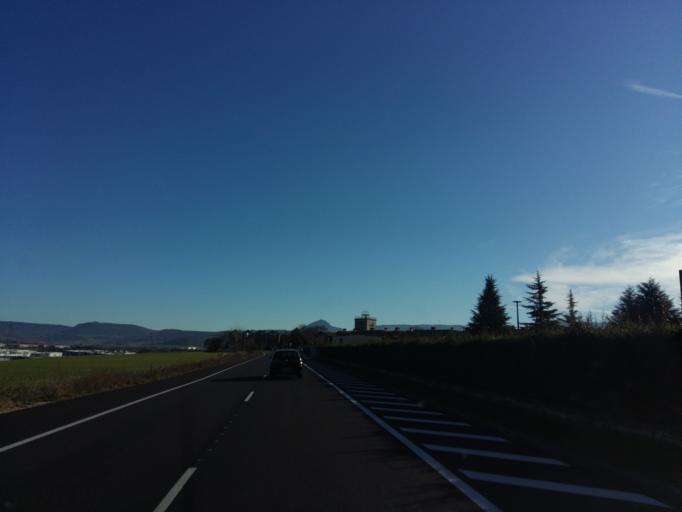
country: ES
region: Navarre
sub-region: Provincia de Navarra
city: Iturrama
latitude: 42.7903
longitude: -1.6481
